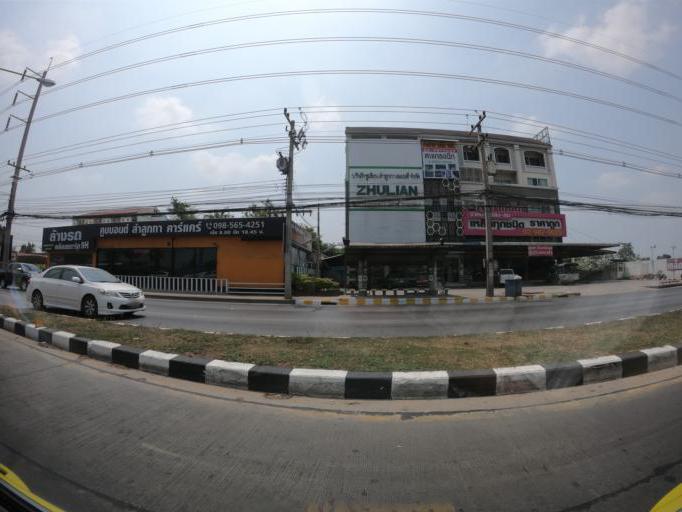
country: TH
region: Bangkok
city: Khlong Sam Wa
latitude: 13.8672
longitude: 100.7250
